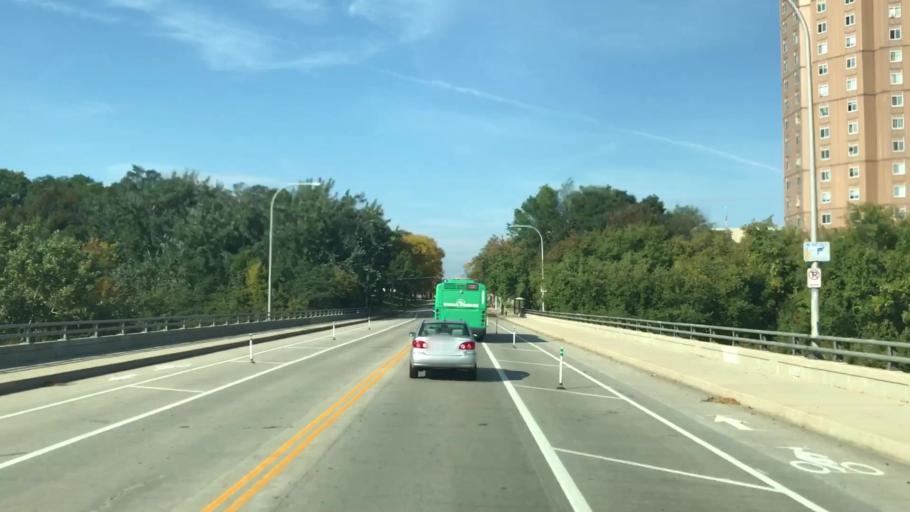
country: US
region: Wisconsin
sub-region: Milwaukee County
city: Shorewood
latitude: 43.0711
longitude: -87.8932
